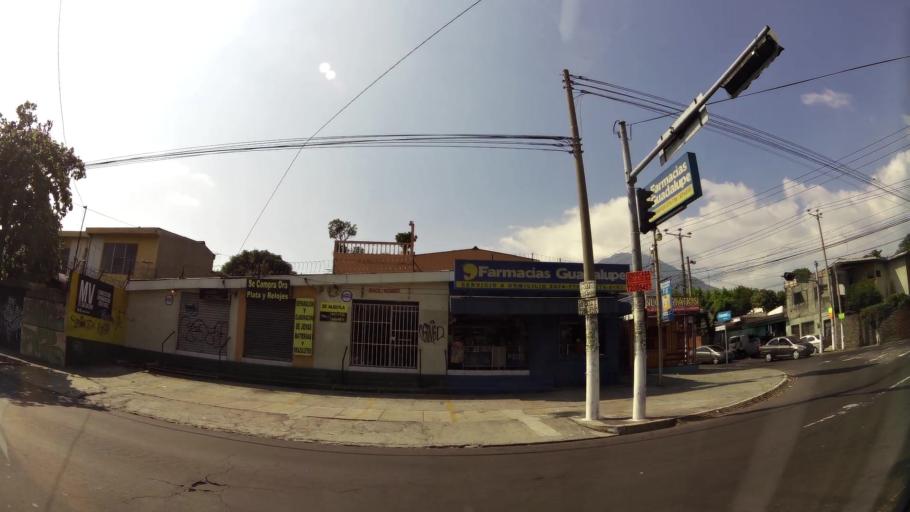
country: SV
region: San Salvador
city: Mejicanos
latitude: 13.7230
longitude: -89.2167
